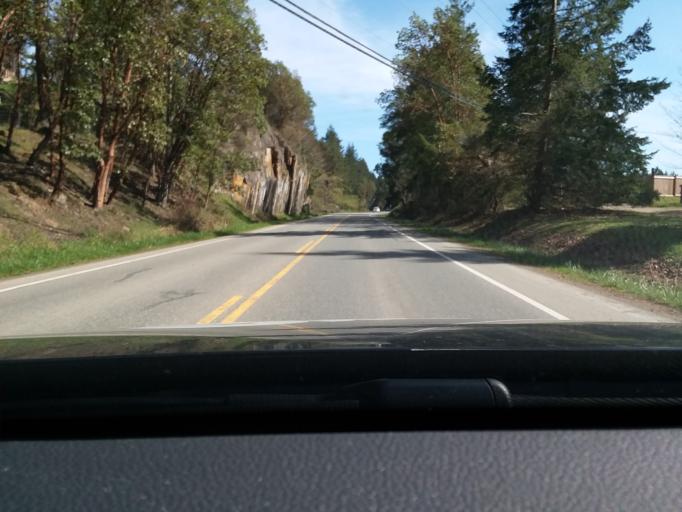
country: CA
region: British Columbia
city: North Saanich
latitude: 48.8558
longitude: -123.4765
